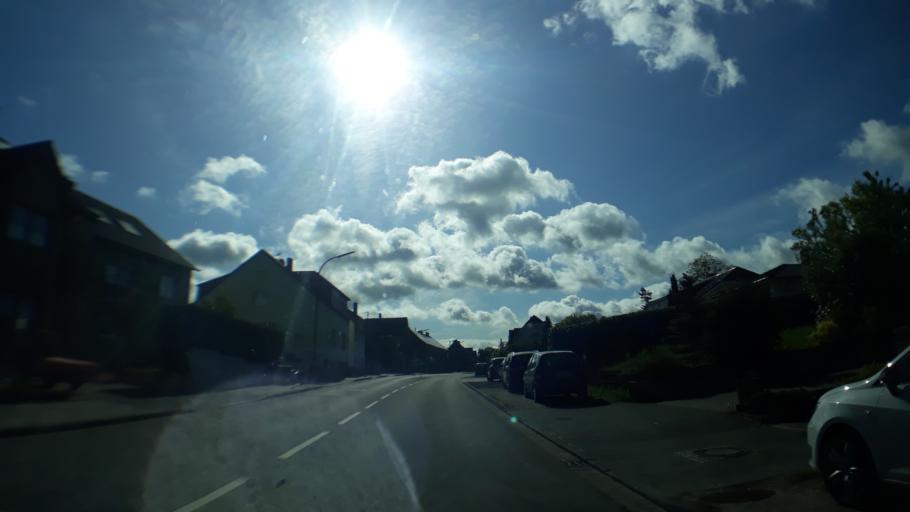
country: DE
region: North Rhine-Westphalia
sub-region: Regierungsbezirk Koln
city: Euskirchen
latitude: 50.6636
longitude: 6.7361
